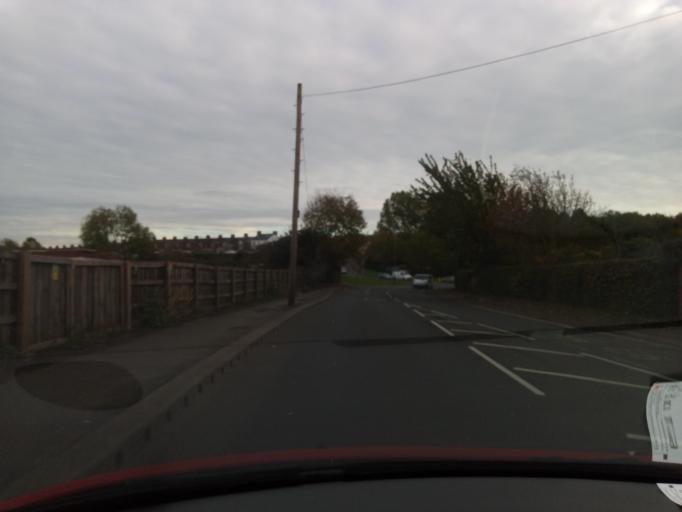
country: GB
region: England
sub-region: County Durham
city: Bishop Auckland
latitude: 54.6460
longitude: -1.6598
